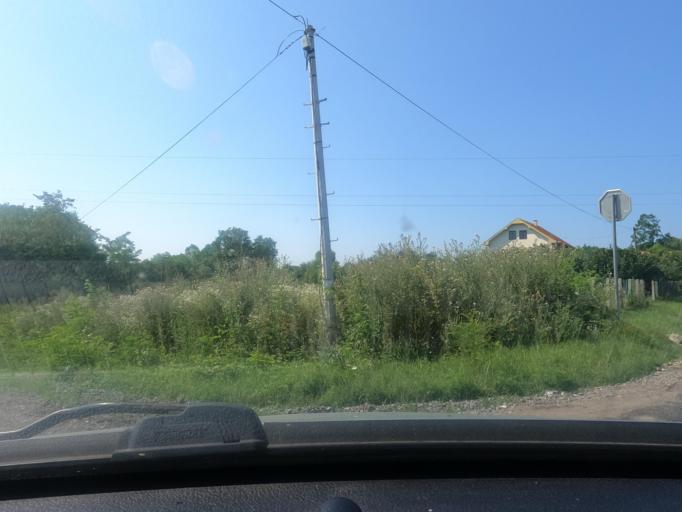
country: RS
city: Kozjak
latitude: 44.5708
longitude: 19.2862
